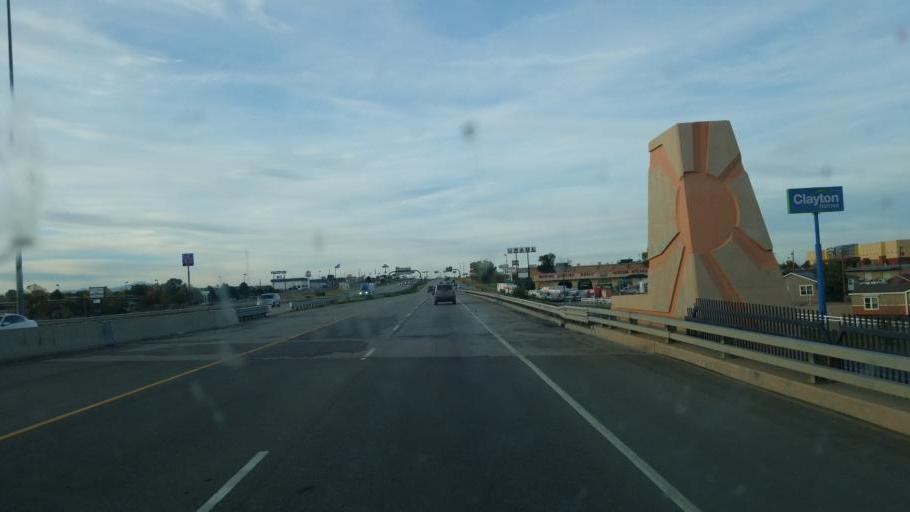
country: US
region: Colorado
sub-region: Pueblo County
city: Pueblo
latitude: 38.3078
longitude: -104.6137
